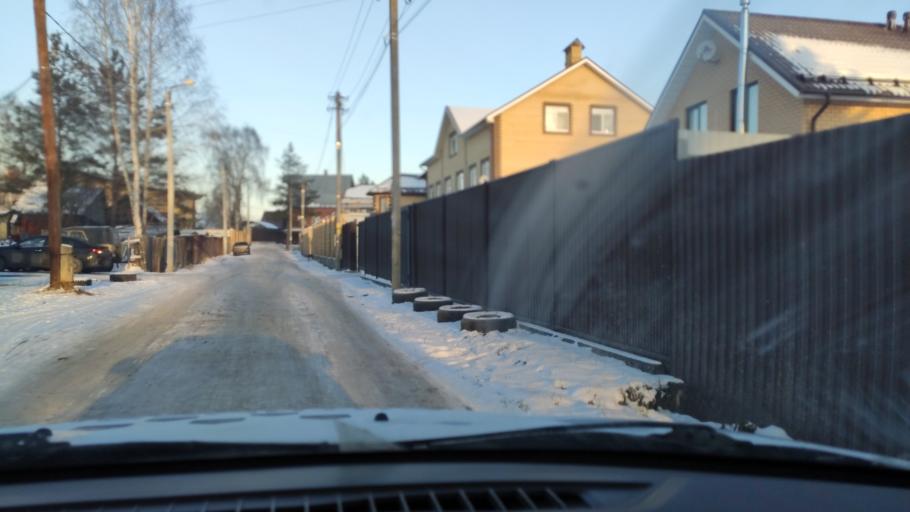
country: RU
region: Perm
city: Perm
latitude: 58.0308
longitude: 56.2293
